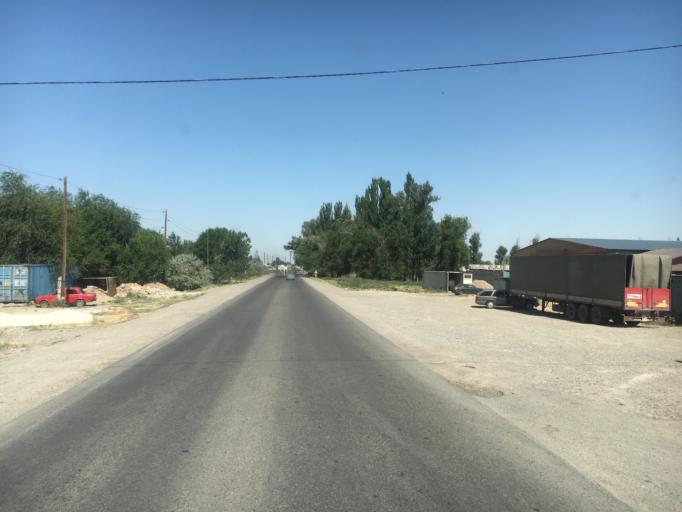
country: KZ
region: Zhambyl
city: Taraz
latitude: 42.9433
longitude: 71.4122
